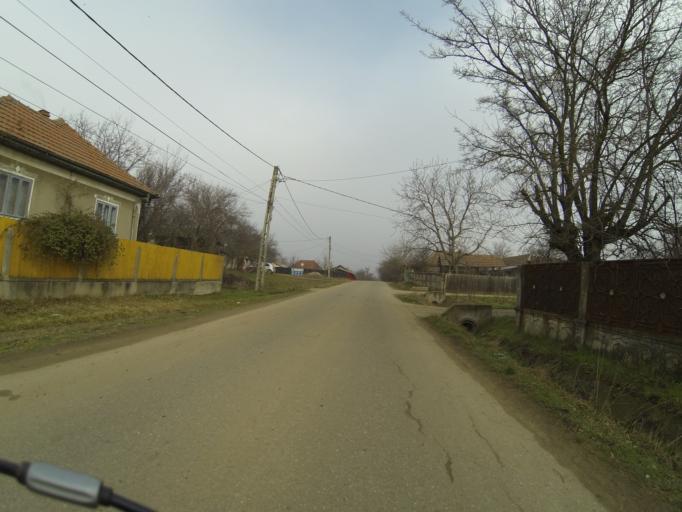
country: RO
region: Mehedinti
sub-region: Comuna Balacita
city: Gvardinita
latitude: 44.3921
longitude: 23.1430
